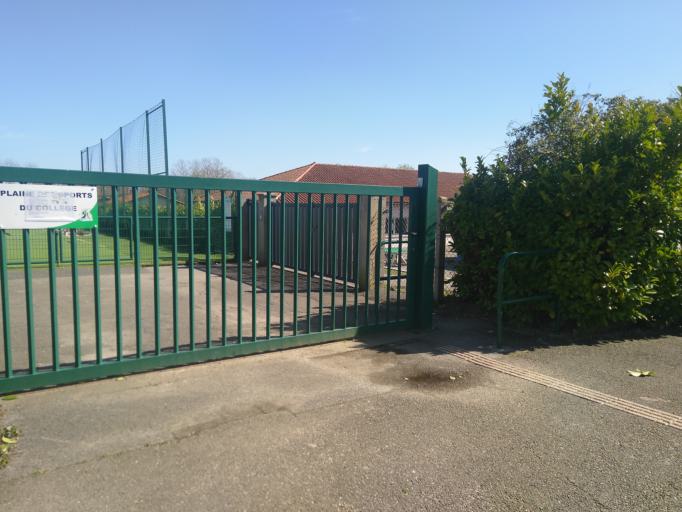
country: FR
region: Aquitaine
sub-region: Departement des Landes
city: Saint-Martin-de-Seignanx
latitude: 43.5408
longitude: -1.3856
